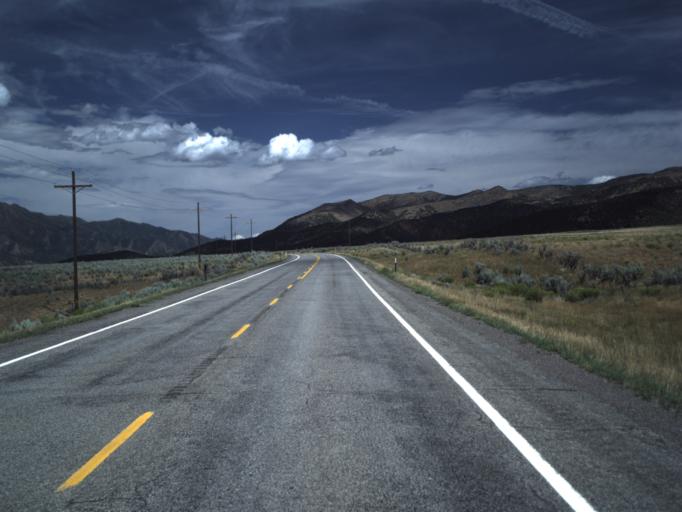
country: US
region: Utah
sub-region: Sanpete County
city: Fairview
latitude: 39.8365
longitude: -111.5124
